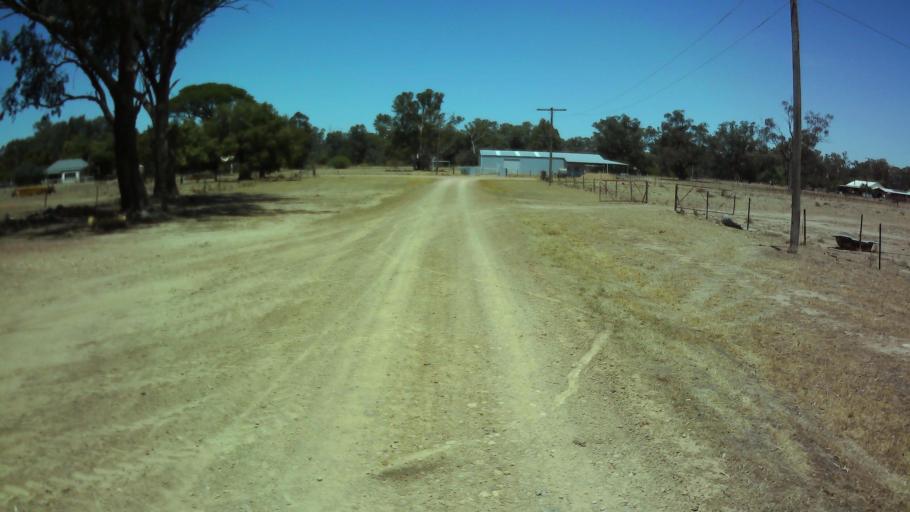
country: AU
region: New South Wales
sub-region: Weddin
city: Grenfell
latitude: -34.0366
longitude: 147.9290
